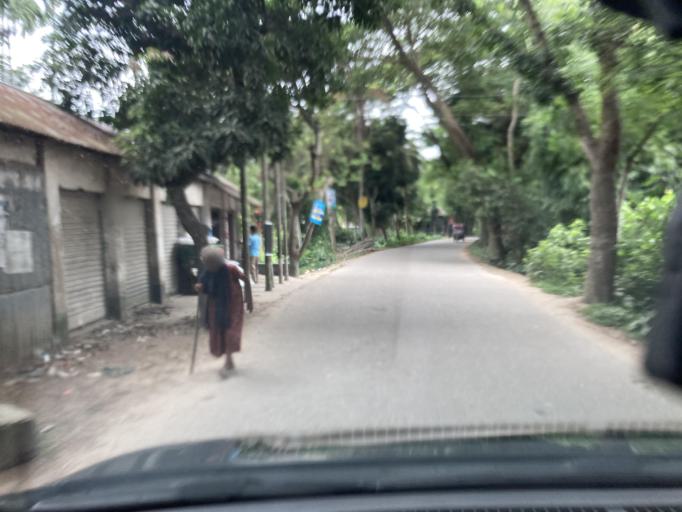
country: BD
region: Dhaka
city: Dohar
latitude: 23.7975
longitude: 90.0487
